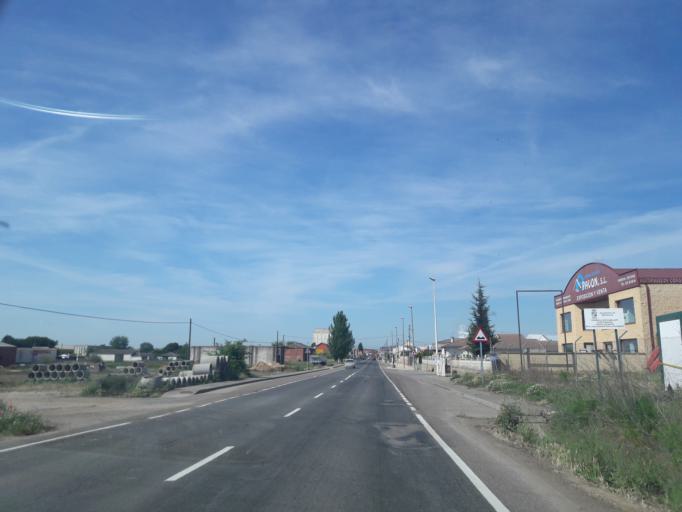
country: ES
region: Castille and Leon
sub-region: Provincia de Salamanca
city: Babilafuente
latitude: 40.9774
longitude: -5.4211
